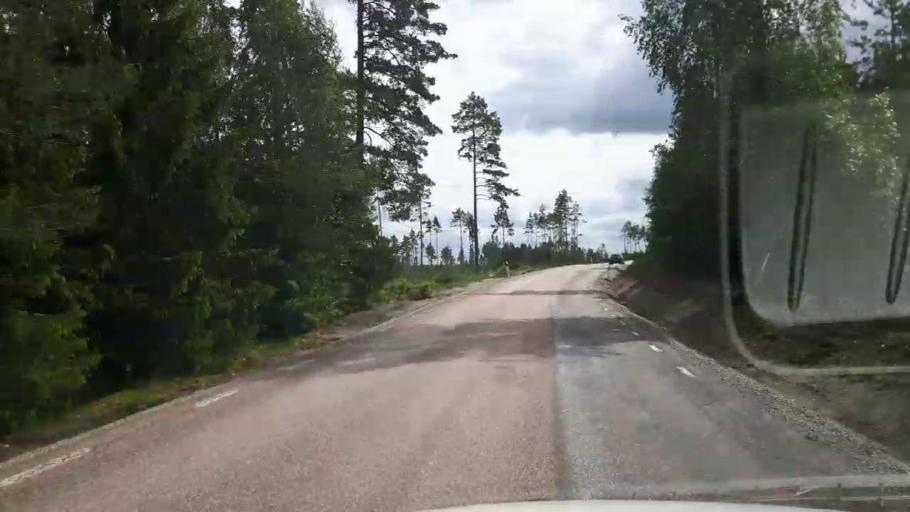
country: SE
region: Vaestmanland
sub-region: Skinnskattebergs Kommun
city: Skinnskatteberg
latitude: 59.8253
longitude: 15.8352
